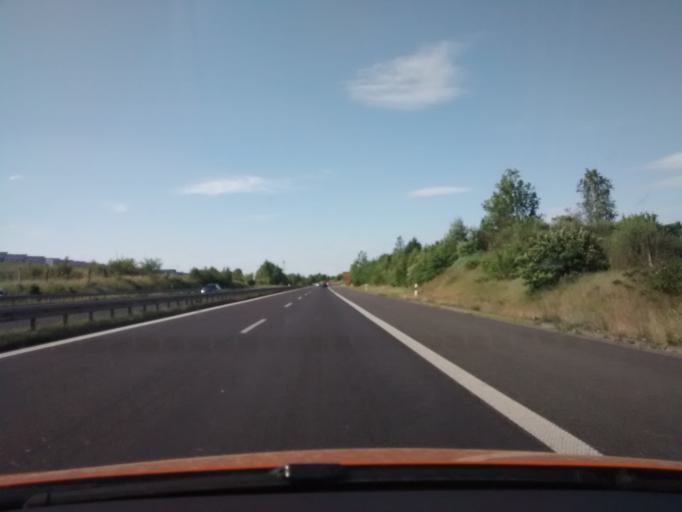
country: DE
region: Brandenburg
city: Grossbeeren
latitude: 52.3372
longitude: 13.2829
